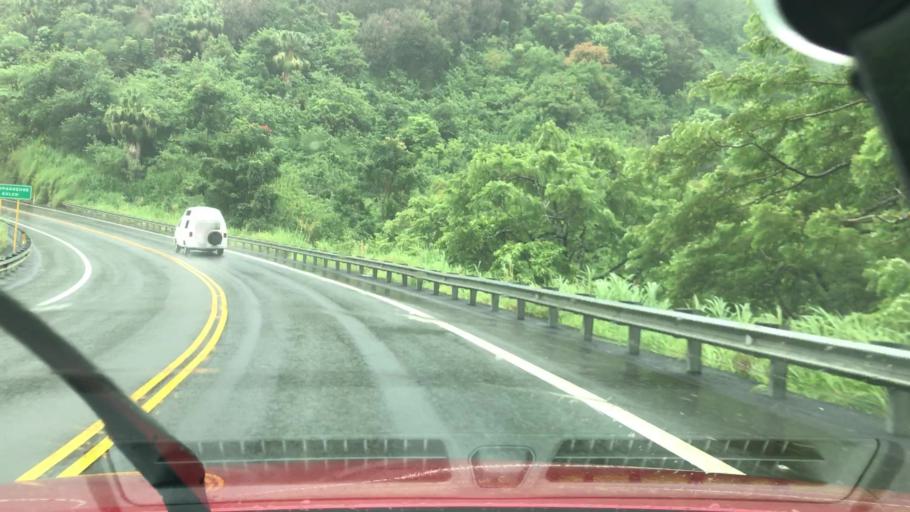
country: US
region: Hawaii
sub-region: Hawaii County
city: Pepeekeo
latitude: 19.9871
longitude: -155.2492
